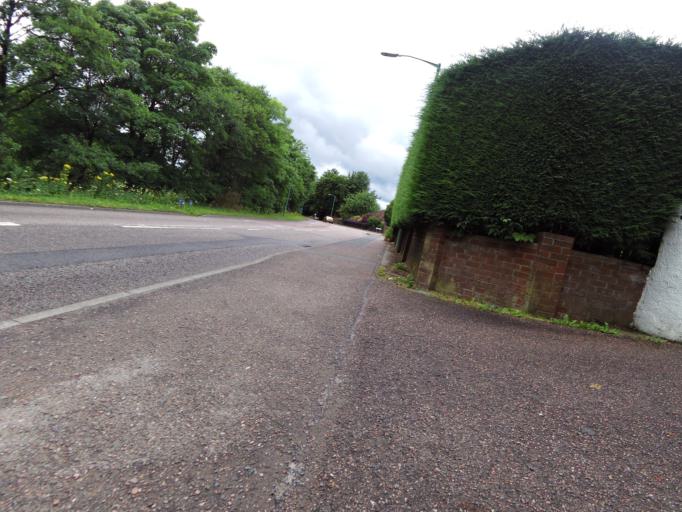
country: GB
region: Scotland
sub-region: Highland
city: Fort William
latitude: 56.8354
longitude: -5.0902
